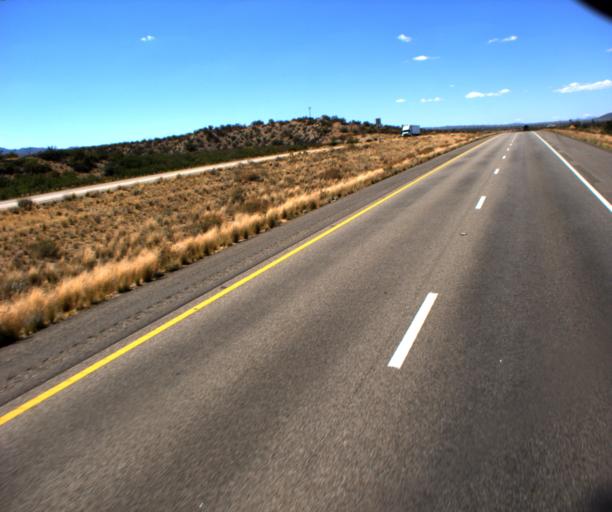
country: US
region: Arizona
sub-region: Yavapai County
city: Bagdad
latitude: 34.8247
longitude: -113.6277
